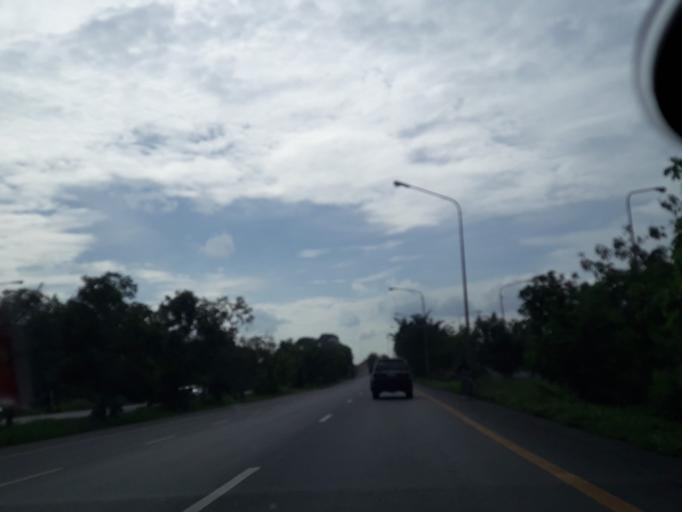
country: TH
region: Sara Buri
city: Saraburi
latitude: 14.5557
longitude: 100.9273
